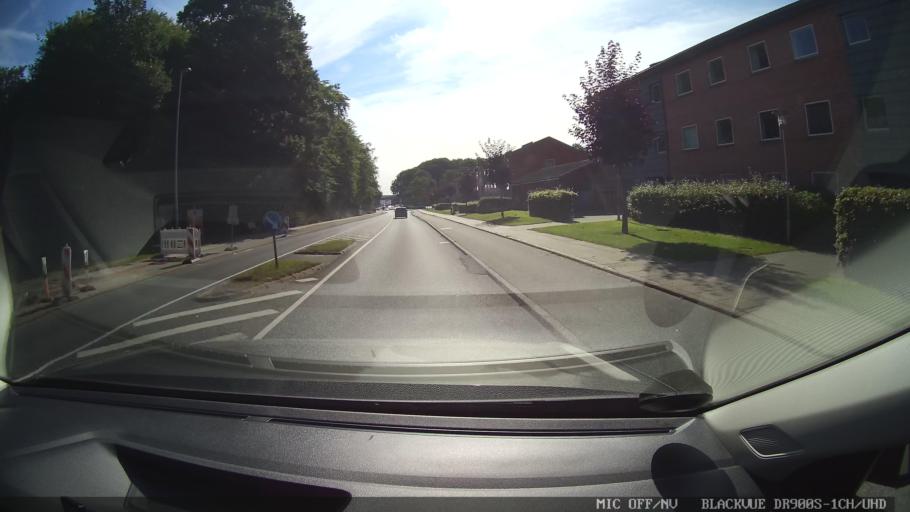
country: DK
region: North Denmark
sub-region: Mariagerfjord Kommune
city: Hadsund
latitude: 56.7187
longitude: 10.1077
